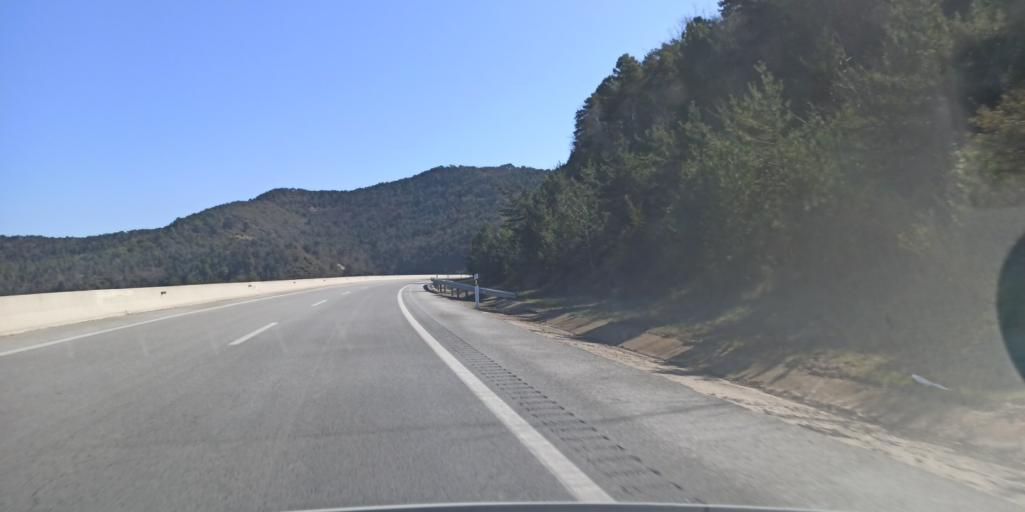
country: ES
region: Catalonia
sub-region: Provincia de Barcelona
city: Orista
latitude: 41.9110
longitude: 2.1215
